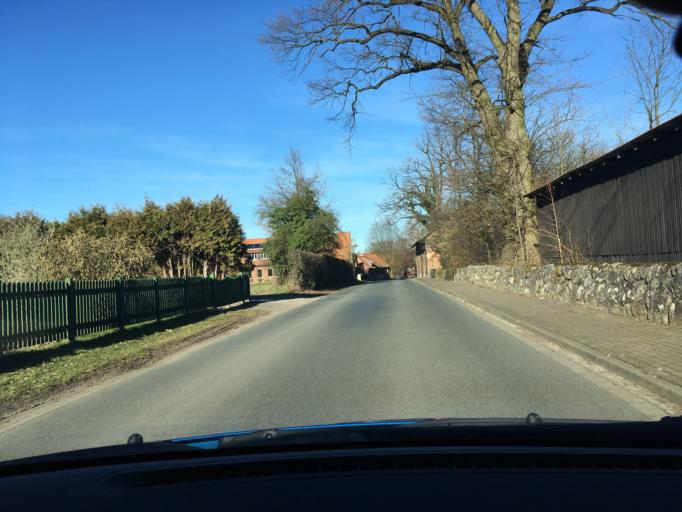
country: DE
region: Lower Saxony
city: Gerdau
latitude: 52.9620
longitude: 10.4556
